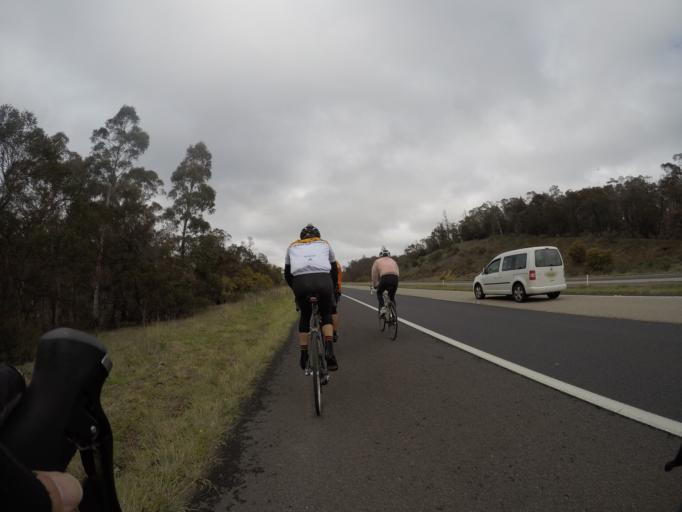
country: AU
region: New South Wales
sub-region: Lithgow
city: Lithgow
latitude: -33.4311
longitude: 150.0748
